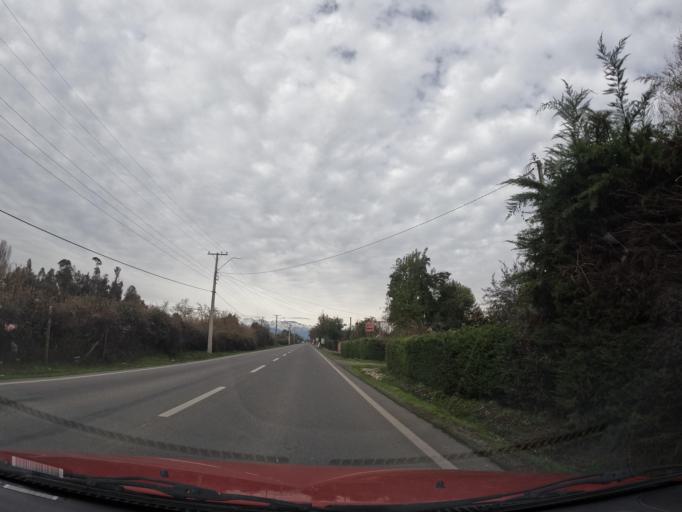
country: CL
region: Maule
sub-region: Provincia de Linares
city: Linares
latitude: -35.8821
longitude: -71.5407
